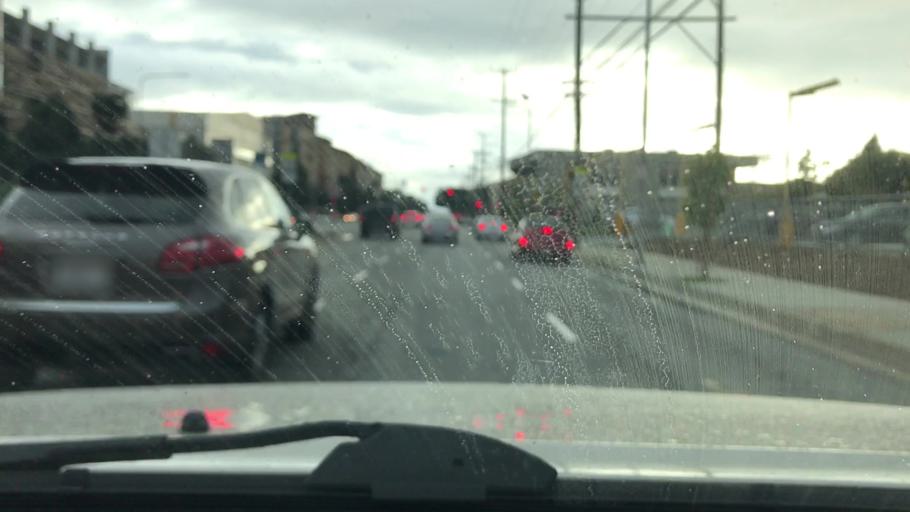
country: US
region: California
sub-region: Los Angeles County
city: Marina del Rey
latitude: 33.9779
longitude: -118.4172
